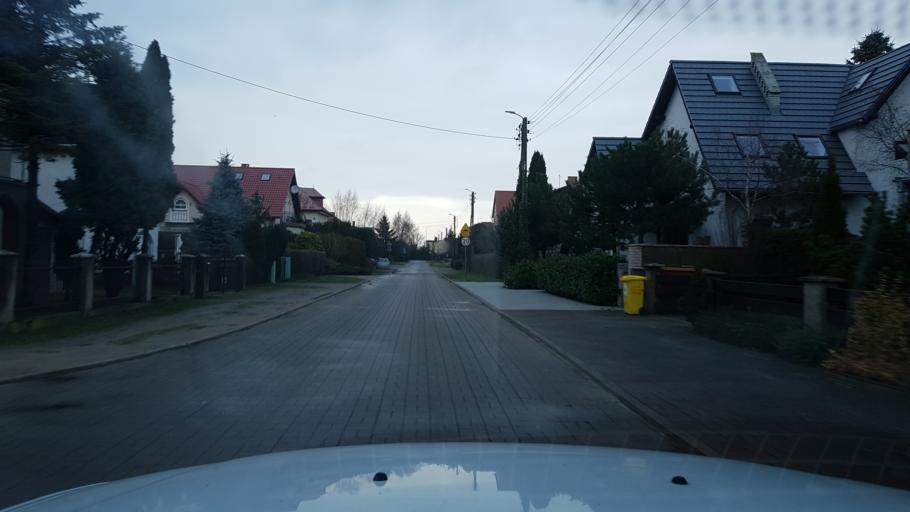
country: PL
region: West Pomeranian Voivodeship
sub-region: Powiat kolobrzeski
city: Kolobrzeg
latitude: 54.1598
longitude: 15.5429
